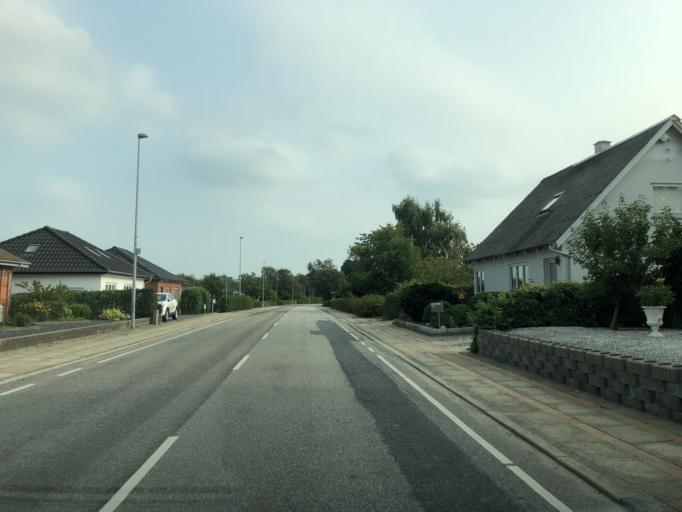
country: DK
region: Central Jutland
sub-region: Ringkobing-Skjern Kommune
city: Videbaek
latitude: 56.0990
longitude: 8.7021
